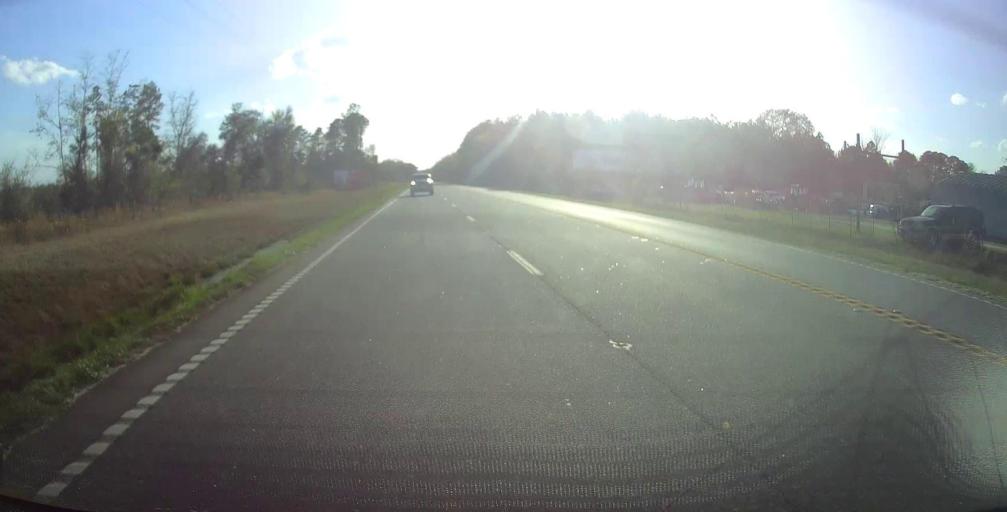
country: US
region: Georgia
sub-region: Tattnall County
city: Reidsville
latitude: 32.1048
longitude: -82.0946
